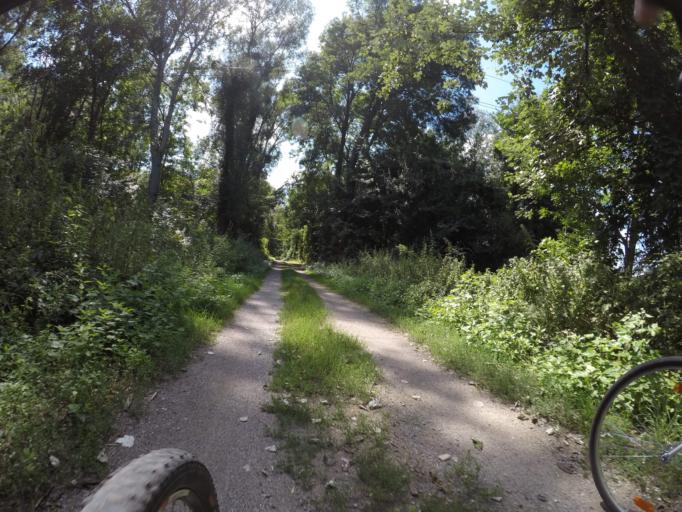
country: AT
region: Lower Austria
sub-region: Politischer Bezirk Ganserndorf
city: Gross-Enzersdorf
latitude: 48.1808
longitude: 16.5194
